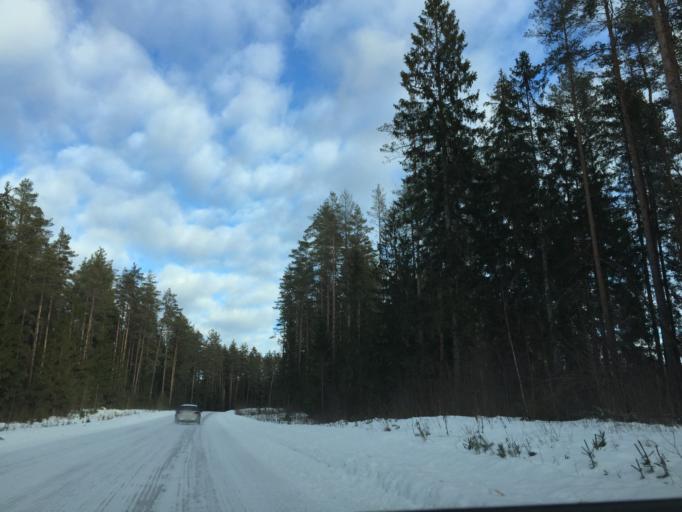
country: LV
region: Ogre
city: Jumprava
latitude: 56.5579
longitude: 24.9026
